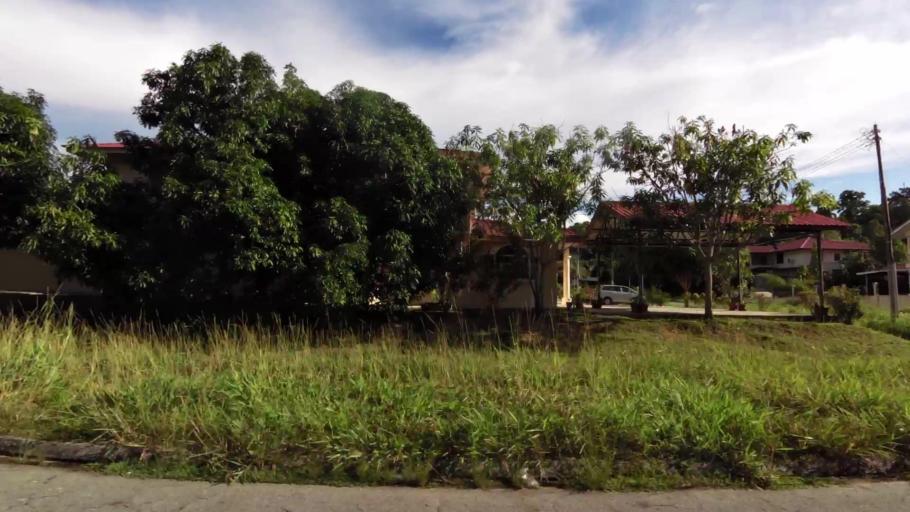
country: BN
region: Brunei and Muara
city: Bandar Seri Begawan
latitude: 4.9703
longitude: 114.9599
